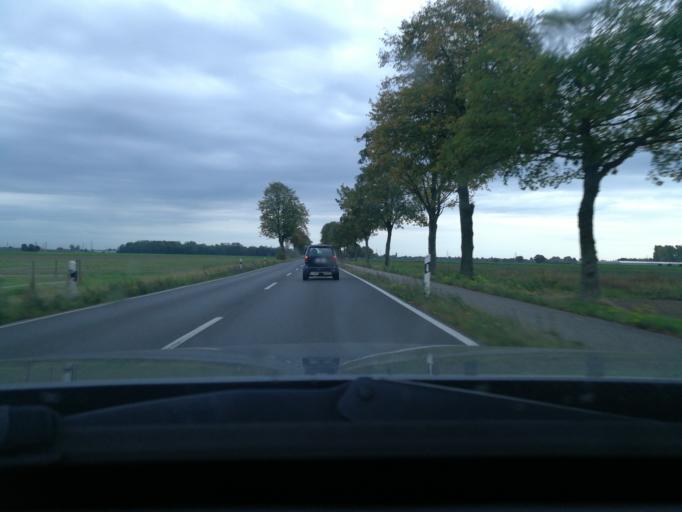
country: DE
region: North Rhine-Westphalia
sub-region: Regierungsbezirk Dusseldorf
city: Dormagen
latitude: 51.1318
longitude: 6.7545
